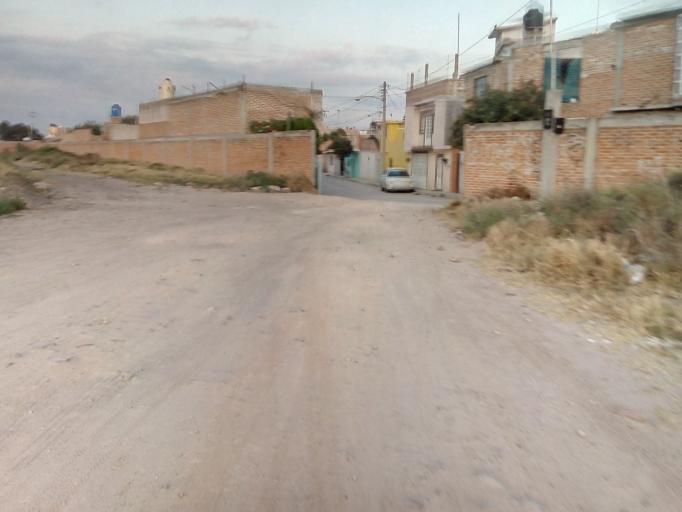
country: MX
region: Guerrero
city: San Luis de la Paz
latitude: 21.2905
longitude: -100.5212
